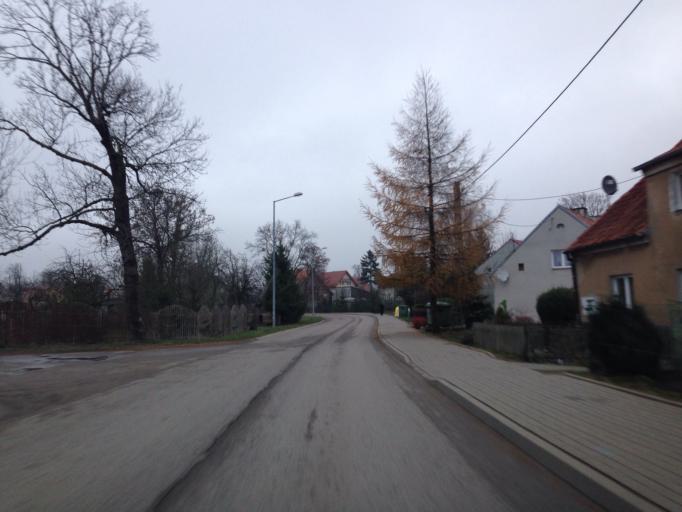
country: PL
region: Warmian-Masurian Voivodeship
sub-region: Powiat ketrzynski
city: Ketrzyn
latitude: 54.0621
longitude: 21.3776
